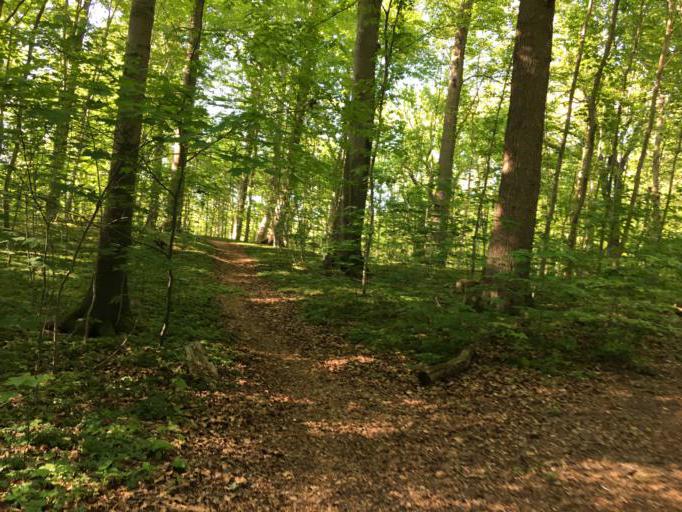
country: DK
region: Capital Region
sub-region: Hillerod Kommune
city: Hillerod
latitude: 55.9251
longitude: 12.3195
